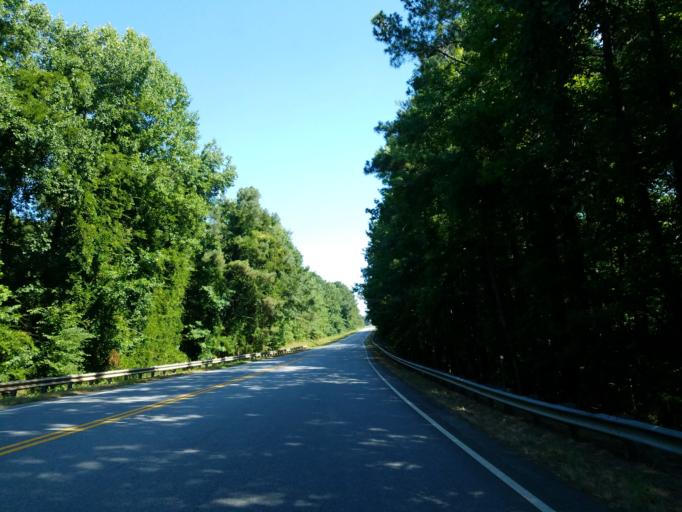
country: US
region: Georgia
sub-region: Crawford County
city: Roberta
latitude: 32.8195
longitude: -84.0550
